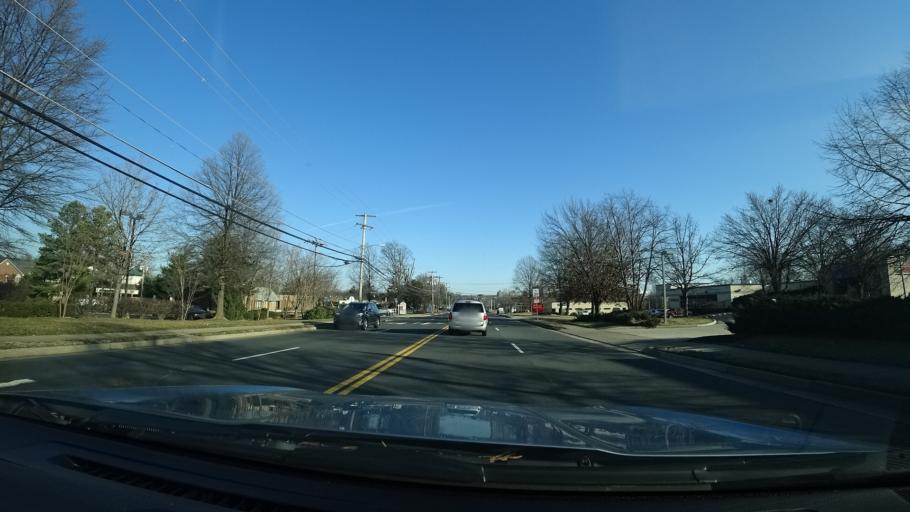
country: US
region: Virginia
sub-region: Fairfax County
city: Herndon
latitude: 38.9689
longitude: -77.3802
